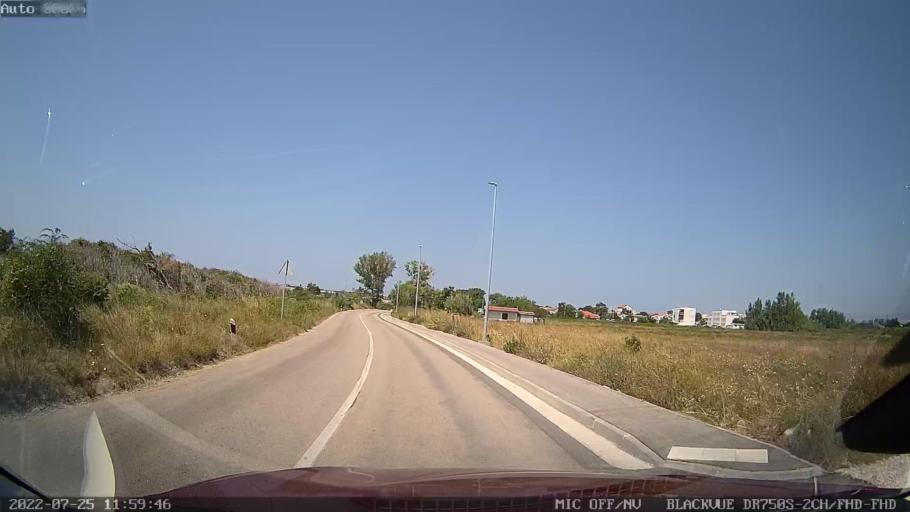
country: HR
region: Zadarska
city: Nin
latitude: 44.2421
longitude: 15.1987
